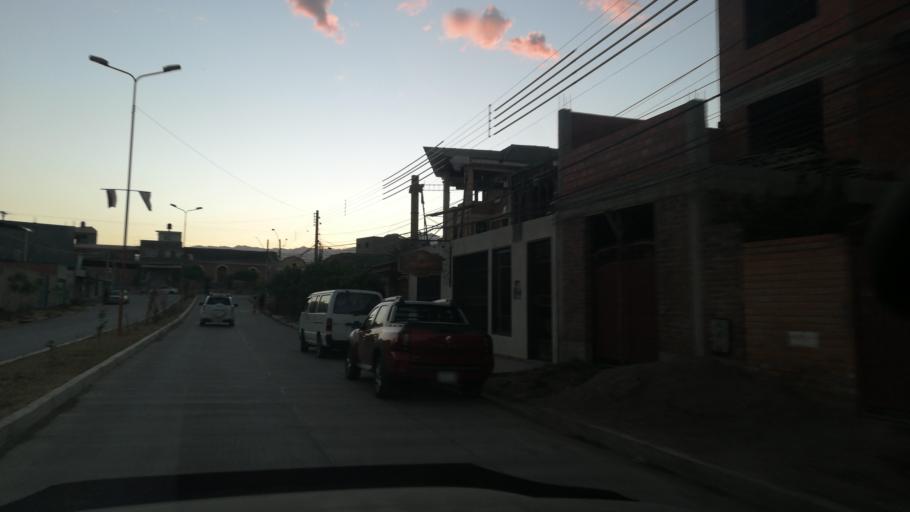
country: BO
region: Cochabamba
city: Cochabamba
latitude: -17.3833
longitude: -66.2203
